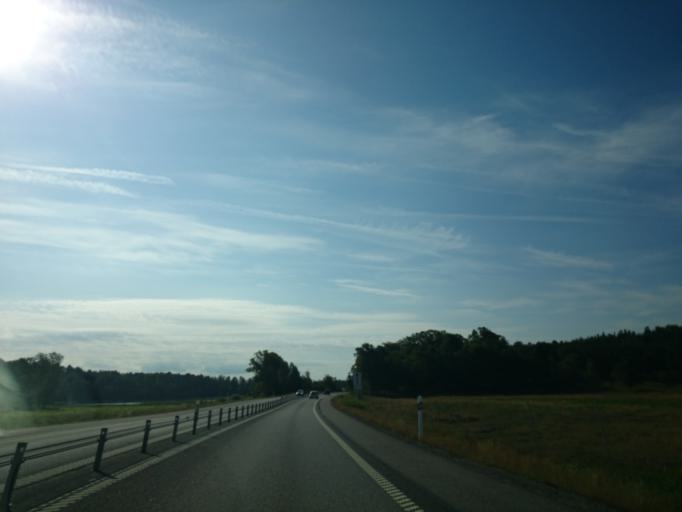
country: SE
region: OEstergoetland
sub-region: Valdemarsviks Kommun
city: Gusum
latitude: 58.3289
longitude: 16.4707
